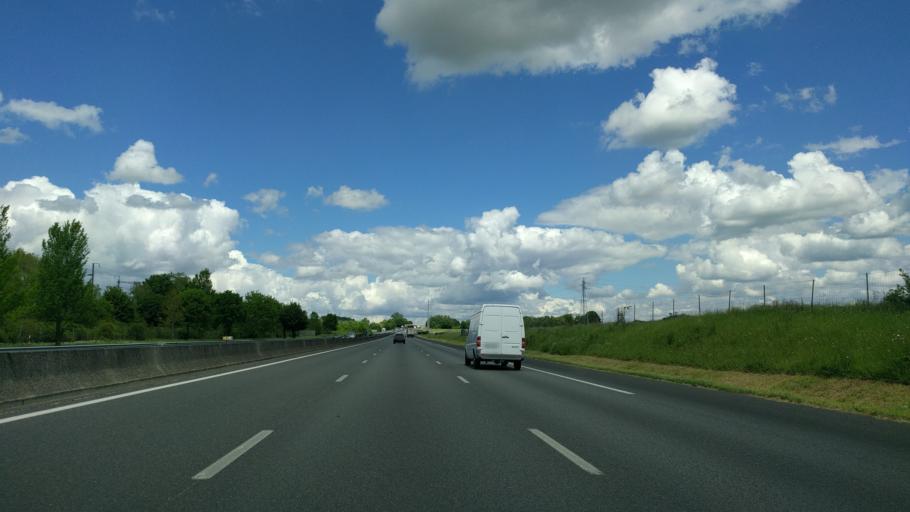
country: FR
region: Picardie
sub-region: Departement de l'Oise
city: Ressons-sur-Matz
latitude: 49.5460
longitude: 2.7293
